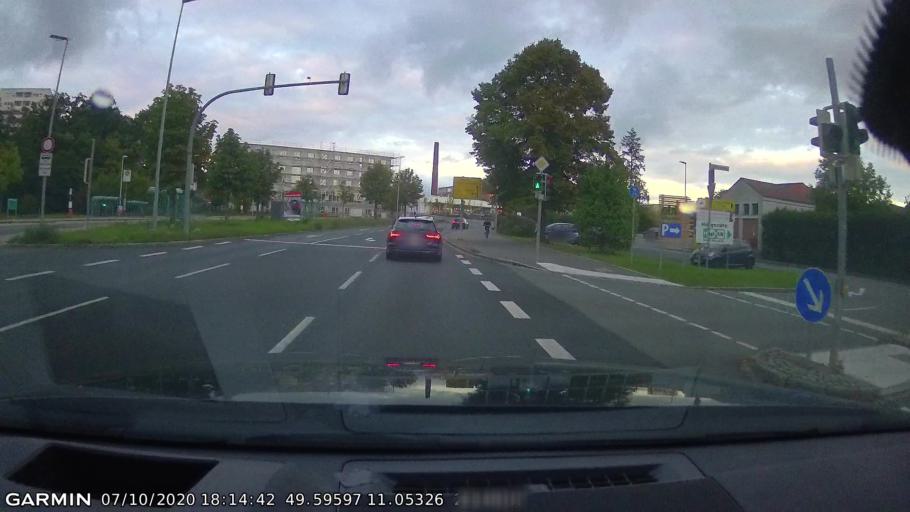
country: DE
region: Bavaria
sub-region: Regierungsbezirk Mittelfranken
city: Buckenhof
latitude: 49.5960
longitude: 11.0533
